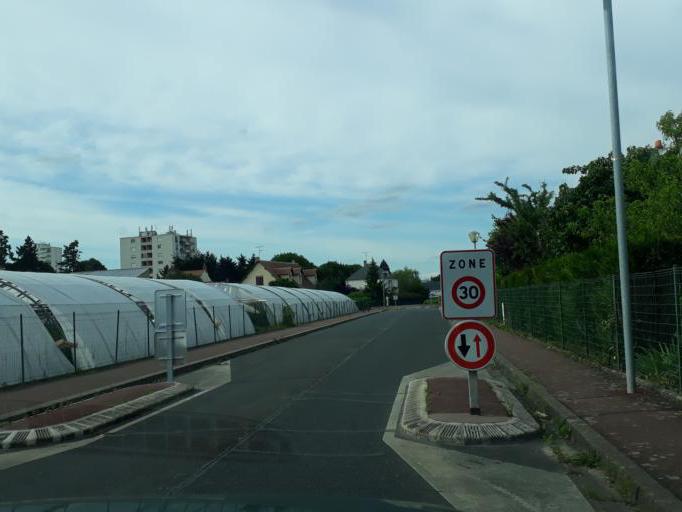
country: FR
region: Centre
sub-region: Departement du Loiret
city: Olivet
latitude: 47.8706
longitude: 1.9063
